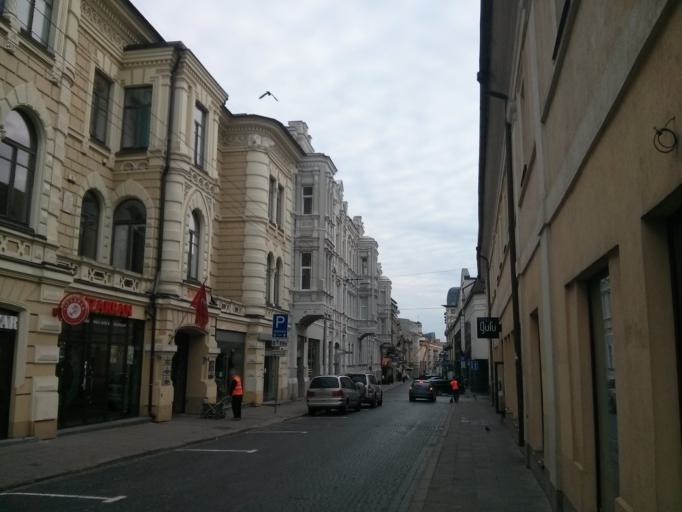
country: LT
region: Vilnius County
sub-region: Vilnius
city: Vilnius
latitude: 54.6842
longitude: 25.2794
